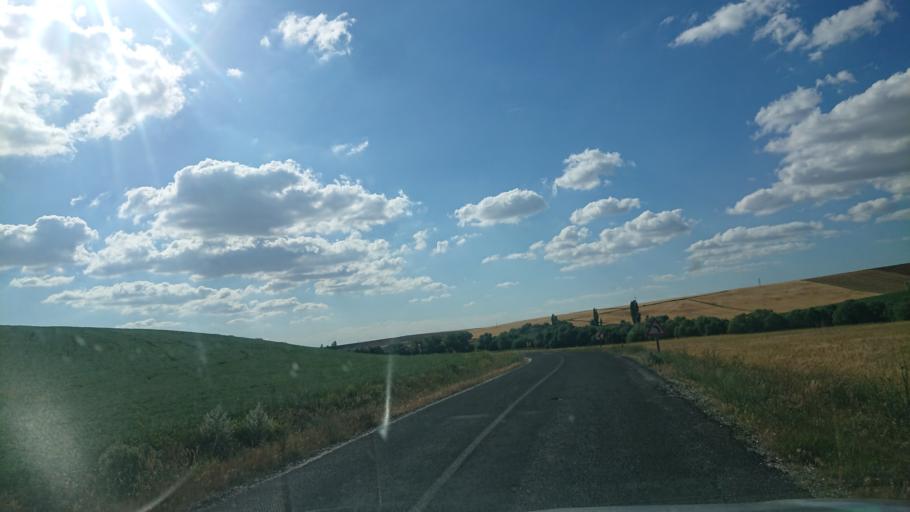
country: TR
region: Aksaray
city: Ortakoy
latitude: 38.7555
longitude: 33.9223
